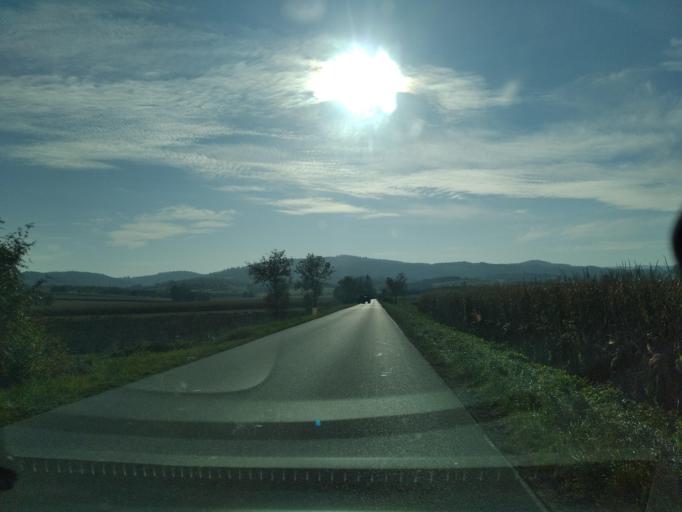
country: PL
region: Subcarpathian Voivodeship
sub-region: Powiat krosnienski
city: Sieniawa
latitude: 49.5627
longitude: 21.9198
